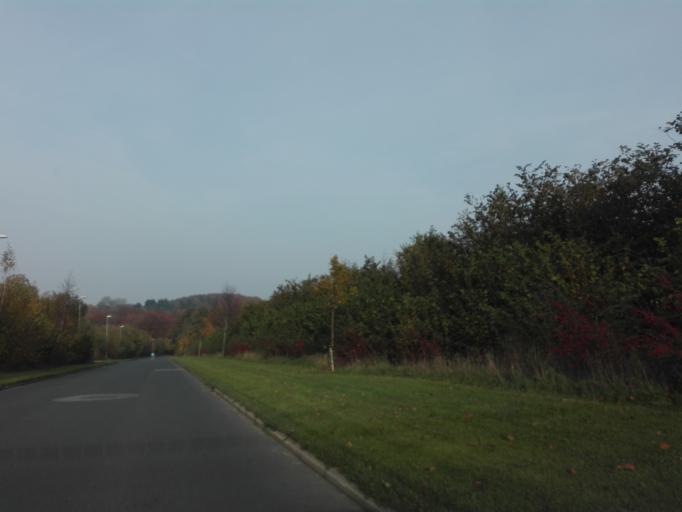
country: DK
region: Central Jutland
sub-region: Odder Kommune
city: Odder
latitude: 55.9817
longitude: 10.1341
